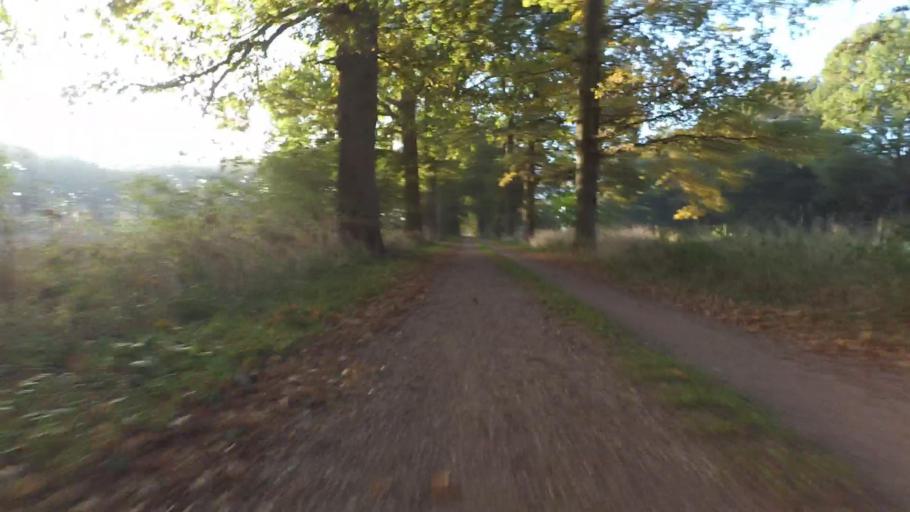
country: NL
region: Utrecht
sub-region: Gemeente De Bilt
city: De Bilt
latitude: 52.1586
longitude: 5.2128
